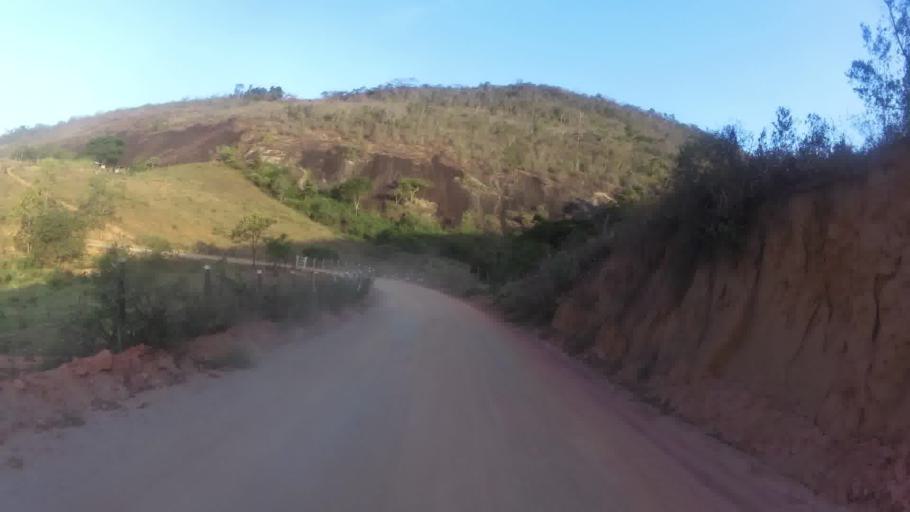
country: BR
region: Espirito Santo
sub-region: Piuma
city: Piuma
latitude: -20.8919
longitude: -40.8031
